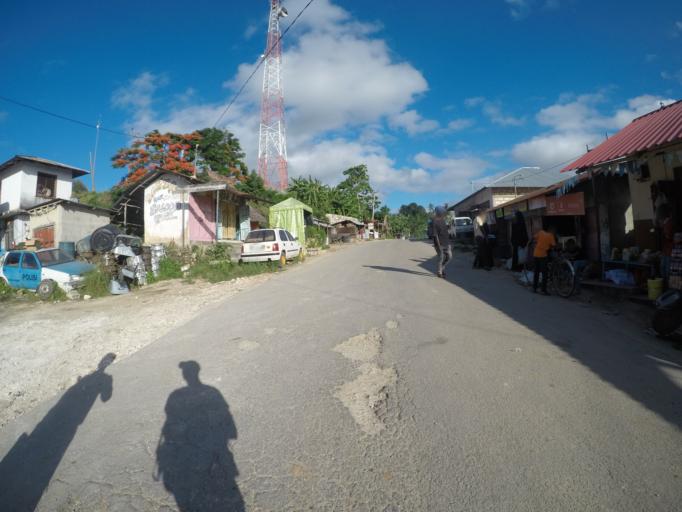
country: TZ
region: Pemba South
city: Mtambile
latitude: -5.3785
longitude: 39.7011
